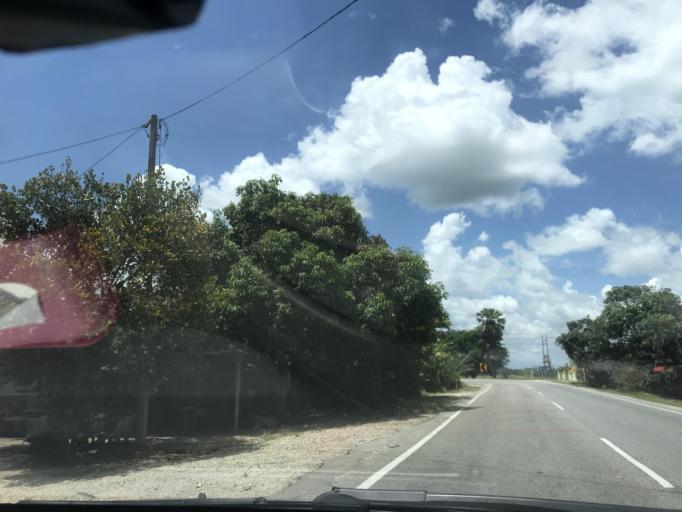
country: MY
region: Kelantan
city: Tumpat
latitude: 6.2028
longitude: 102.1214
